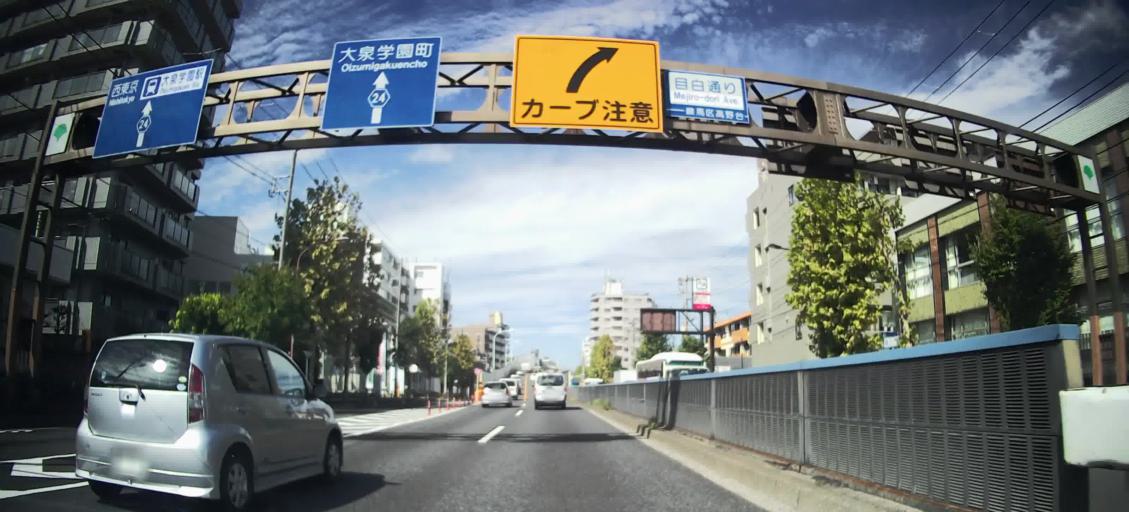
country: JP
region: Saitama
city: Wako
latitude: 35.7493
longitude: 139.6174
